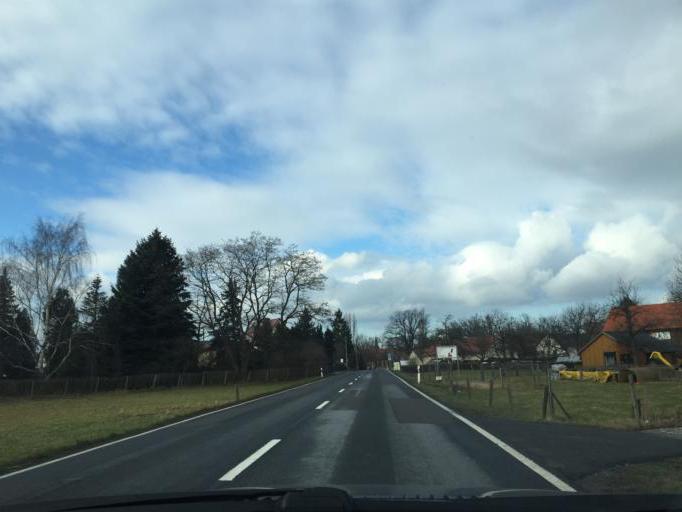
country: DE
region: Saxony
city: Wachau
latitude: 51.1565
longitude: 13.8866
